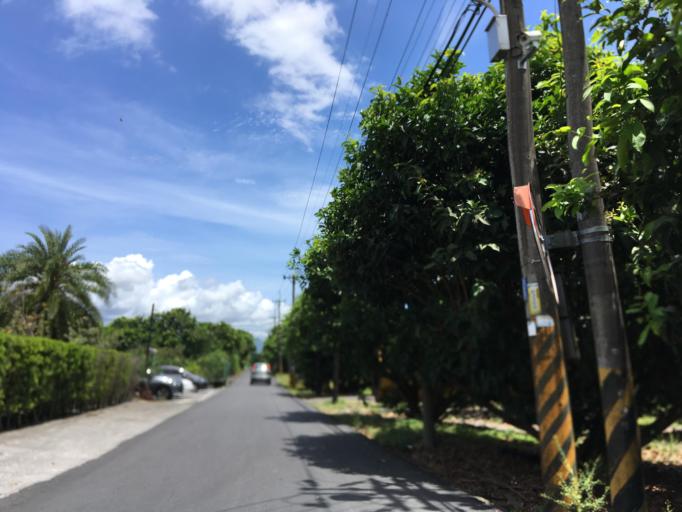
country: TW
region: Taiwan
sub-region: Yilan
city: Yilan
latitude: 24.6385
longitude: 121.7202
